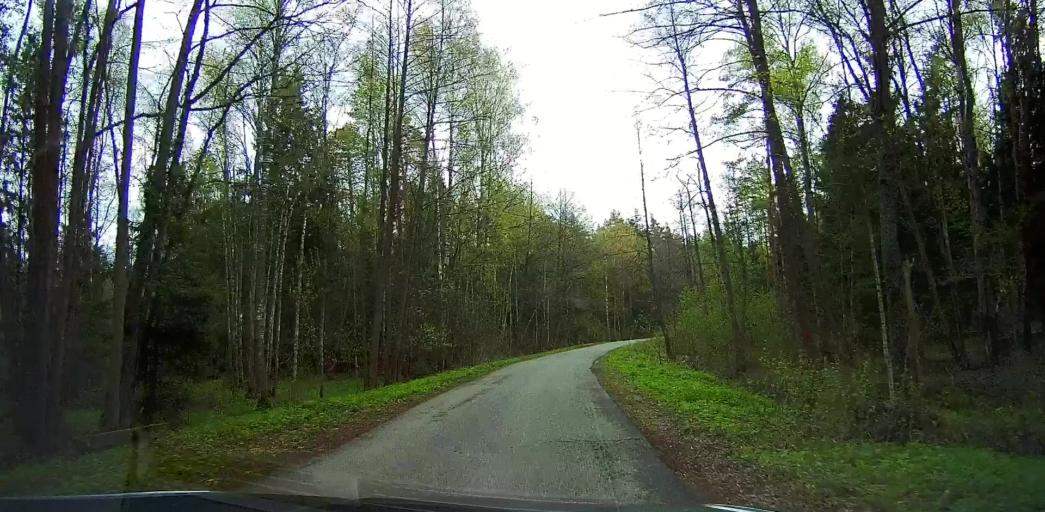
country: RU
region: Moskovskaya
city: Malyshevo
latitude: 55.5427
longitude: 38.3856
